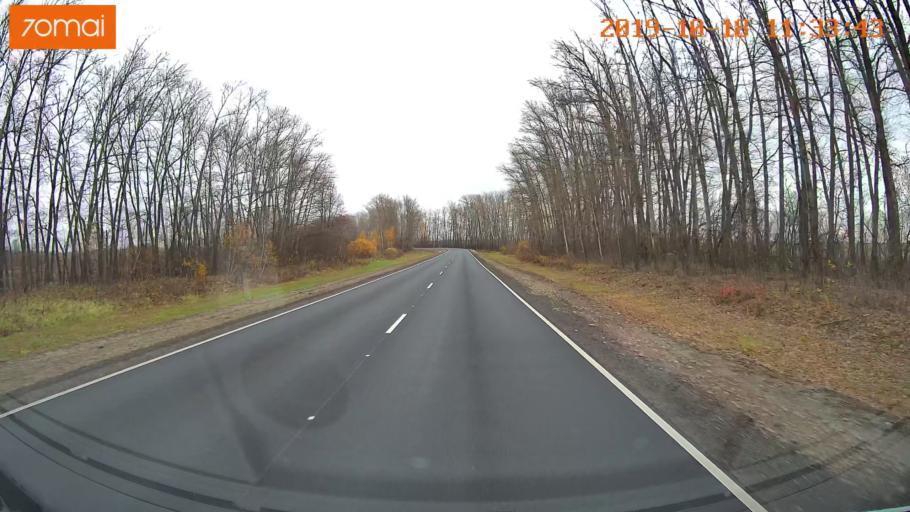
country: RU
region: Rjazan
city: Oktyabr'skiy
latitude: 54.1392
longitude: 38.7468
